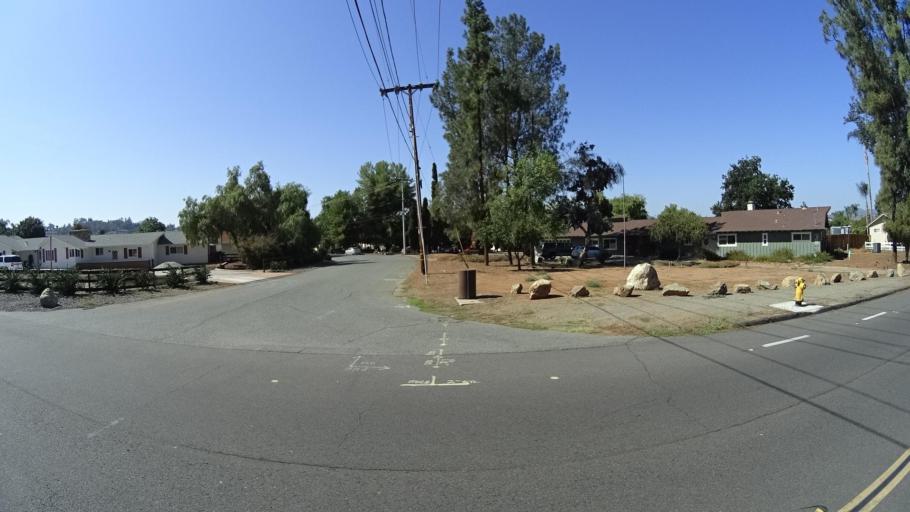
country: US
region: California
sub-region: San Diego County
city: Granite Hills
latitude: 32.7914
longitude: -116.9199
